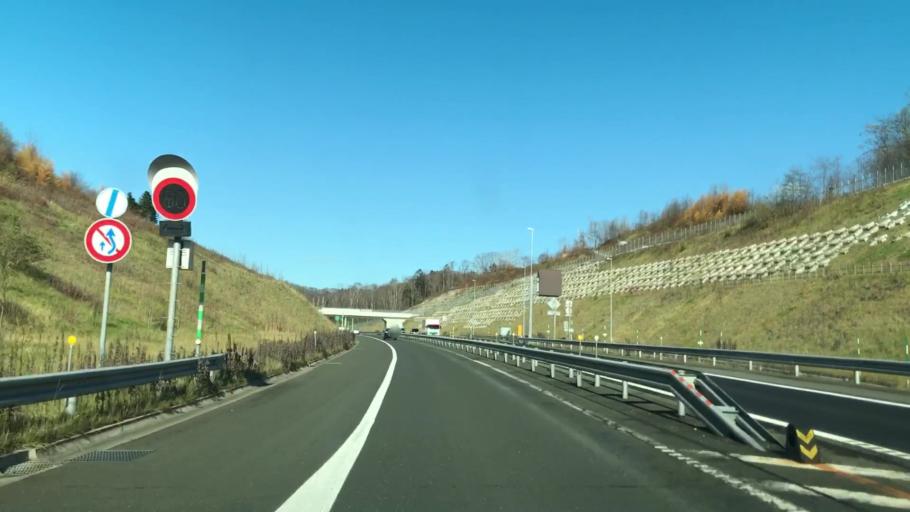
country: JP
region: Hokkaido
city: Shimo-furano
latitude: 42.9809
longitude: 142.4101
